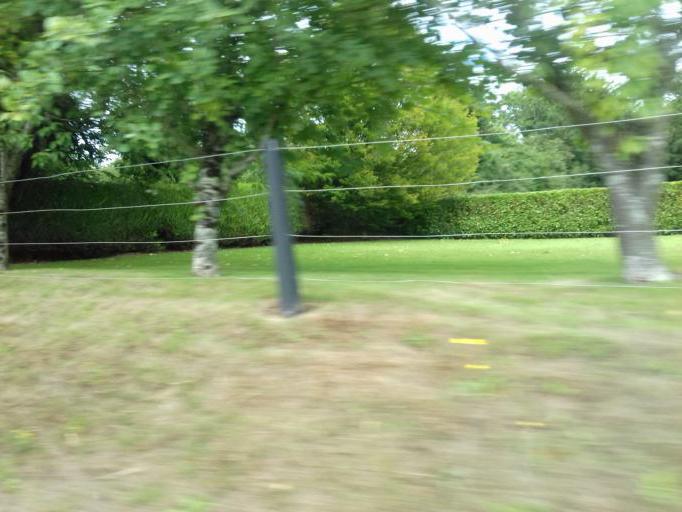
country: IE
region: Leinster
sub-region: Loch Garman
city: Ballinroad
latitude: 52.4833
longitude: -6.4328
